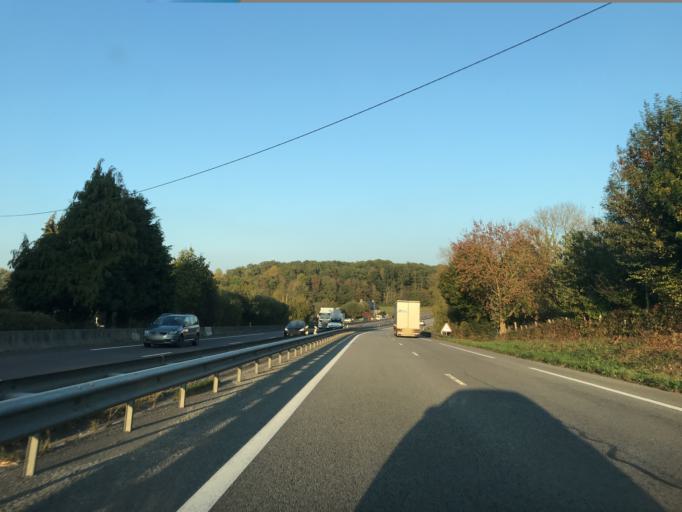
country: FR
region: Lower Normandy
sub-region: Departement de l'Orne
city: Valframbert
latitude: 48.4729
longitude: 0.1818
